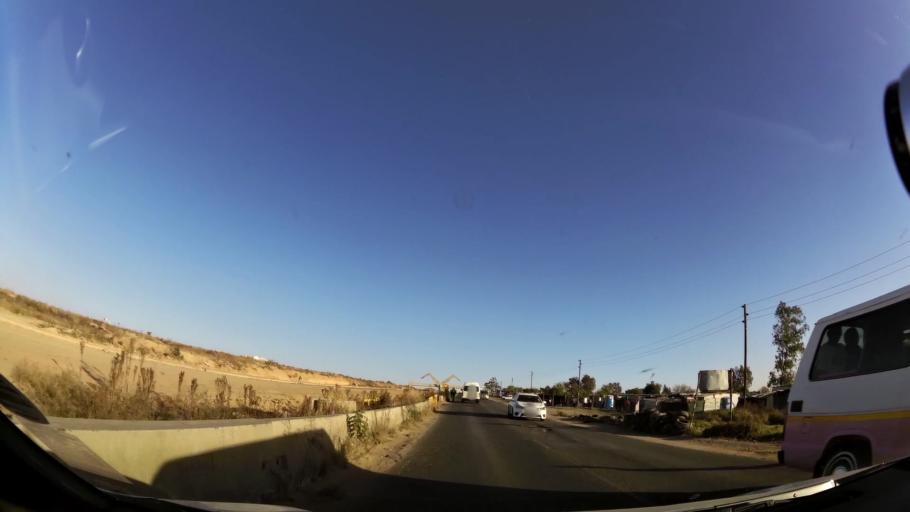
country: ZA
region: Gauteng
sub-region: City of Johannesburg Metropolitan Municipality
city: Diepsloot
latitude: -25.9263
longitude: 28.0224
